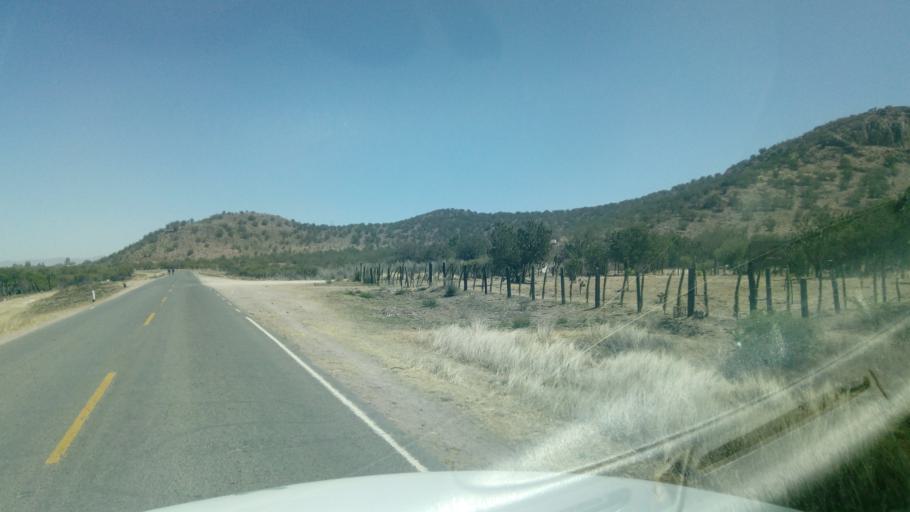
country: MX
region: Durango
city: Victoria de Durango
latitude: 24.1580
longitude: -104.7050
